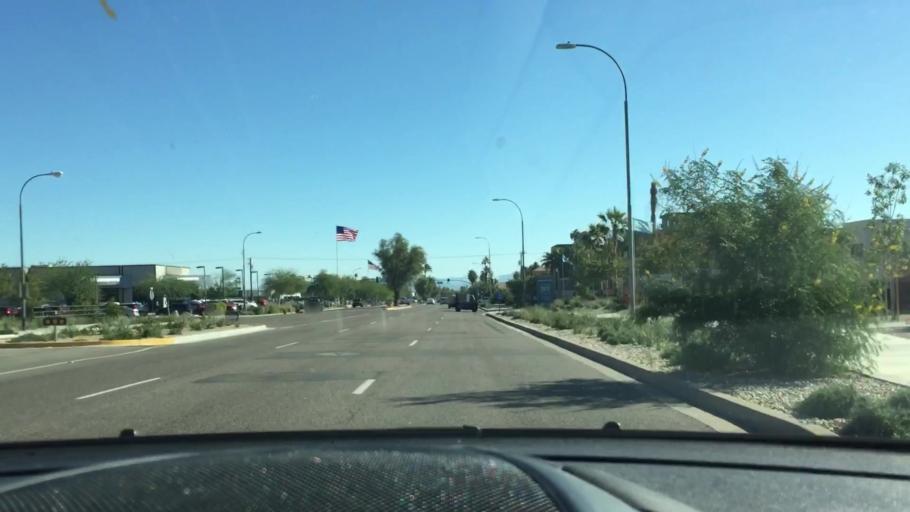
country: US
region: Arizona
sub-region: Maricopa County
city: Tempe Junction
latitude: 33.4656
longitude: -111.9328
